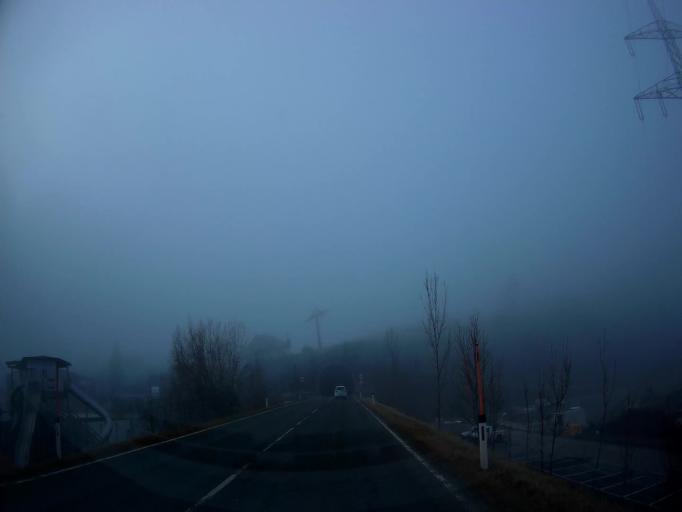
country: AT
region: Salzburg
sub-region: Politischer Bezirk Zell am See
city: Kaprun
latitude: 47.2749
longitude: 12.7564
